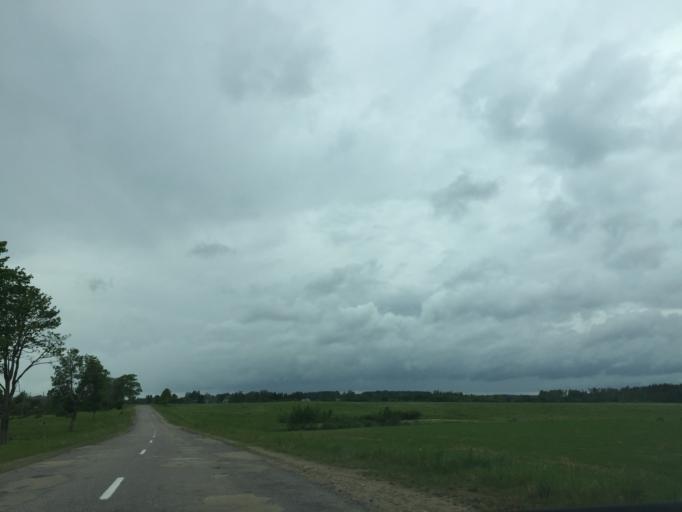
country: LV
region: Varkava
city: Vecvarkava
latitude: 56.1027
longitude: 26.5144
